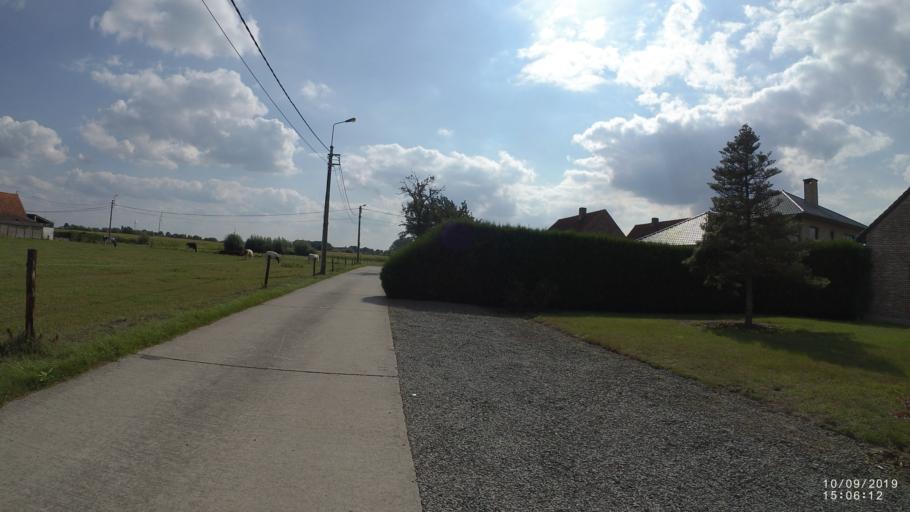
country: BE
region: Flanders
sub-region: Provincie Oost-Vlaanderen
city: Evergem
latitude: 51.1151
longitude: 3.6815
